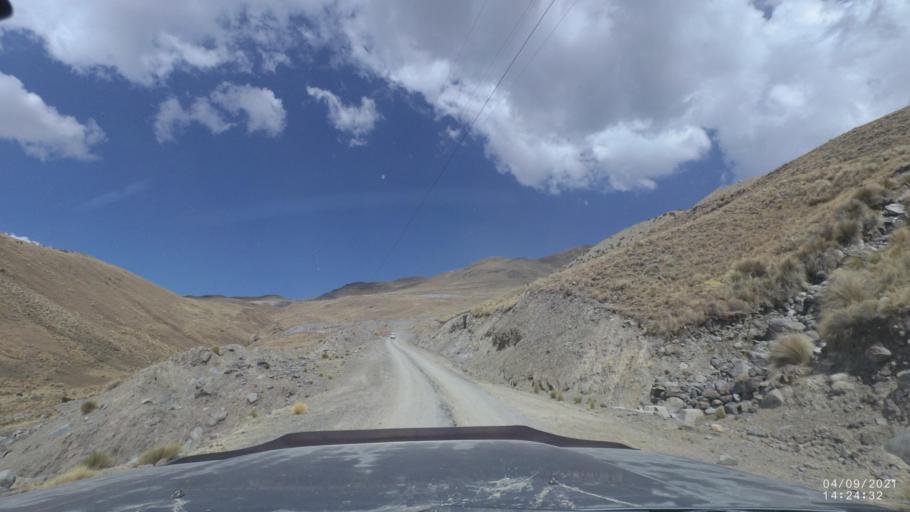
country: BO
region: Cochabamba
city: Sipe Sipe
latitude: -17.2411
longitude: -66.4094
